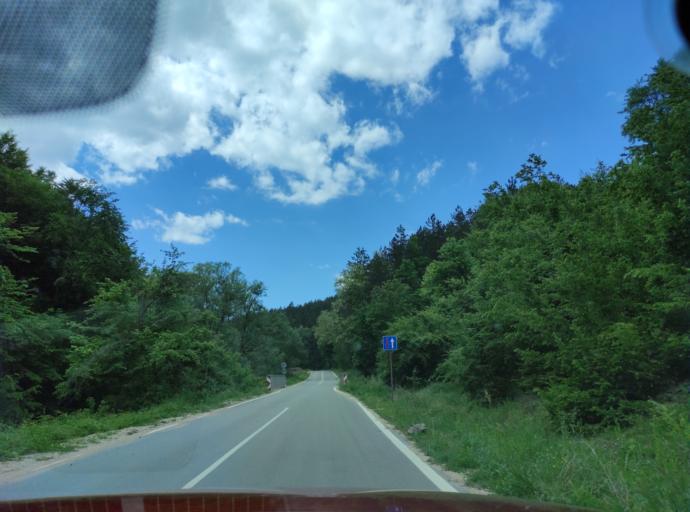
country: BG
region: Montana
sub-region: Obshtina Chiprovtsi
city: Chiprovtsi
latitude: 43.4638
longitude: 22.8812
